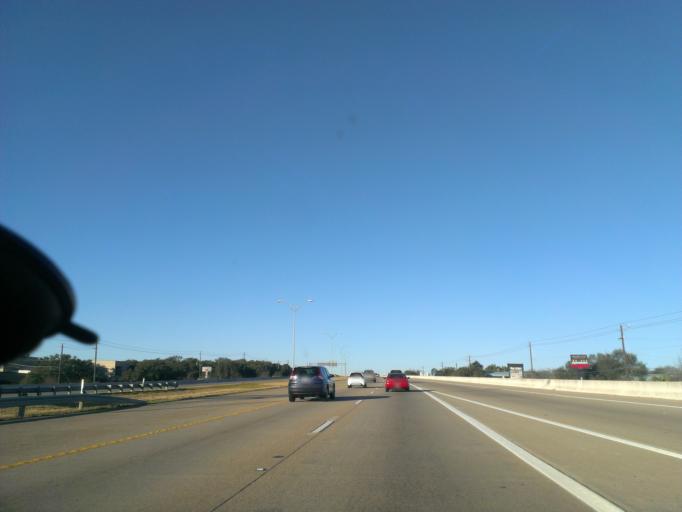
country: US
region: Texas
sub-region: Travis County
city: Barton Creek
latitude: 30.2367
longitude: -97.8450
